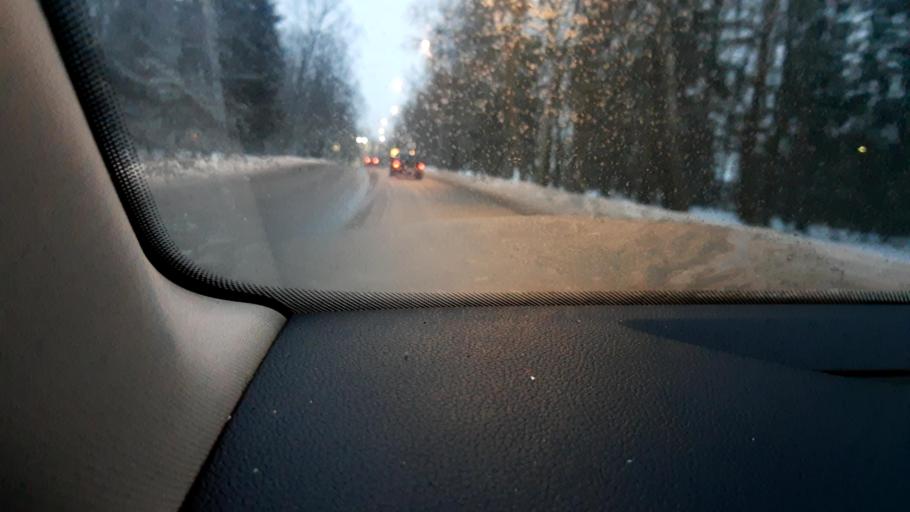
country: RU
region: Moskovskaya
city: Troitsk
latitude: 55.3046
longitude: 37.1906
